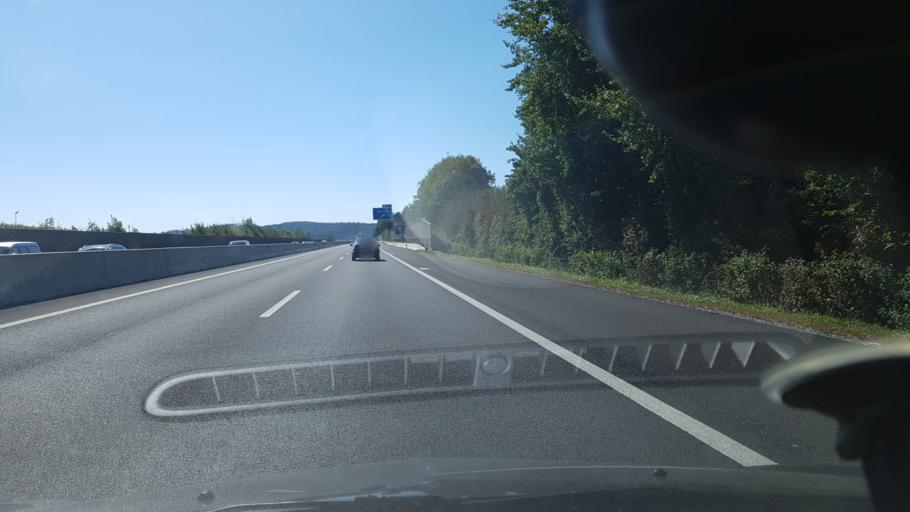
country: AT
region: Styria
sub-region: Politischer Bezirk Leibnitz
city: Weitendorf
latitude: 46.8990
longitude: 15.4720
